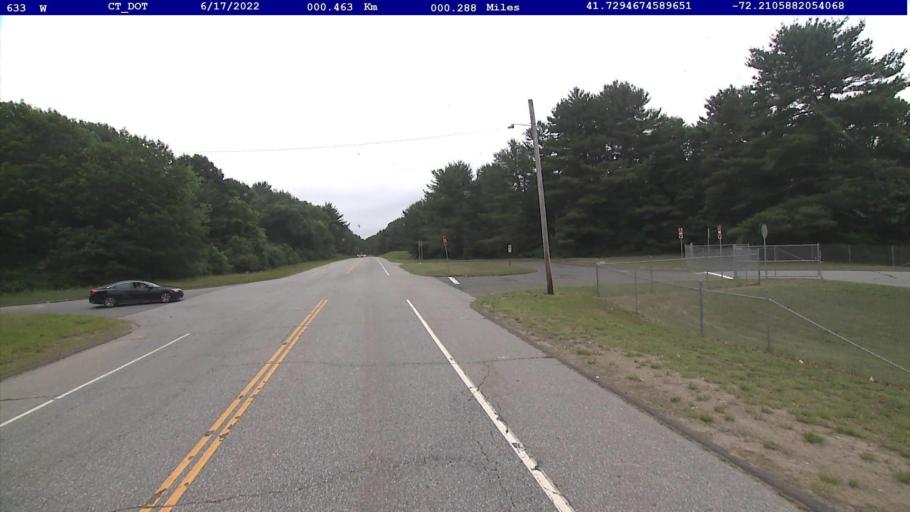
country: US
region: Connecticut
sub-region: Windham County
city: Willimantic
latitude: 41.7294
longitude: -72.2106
